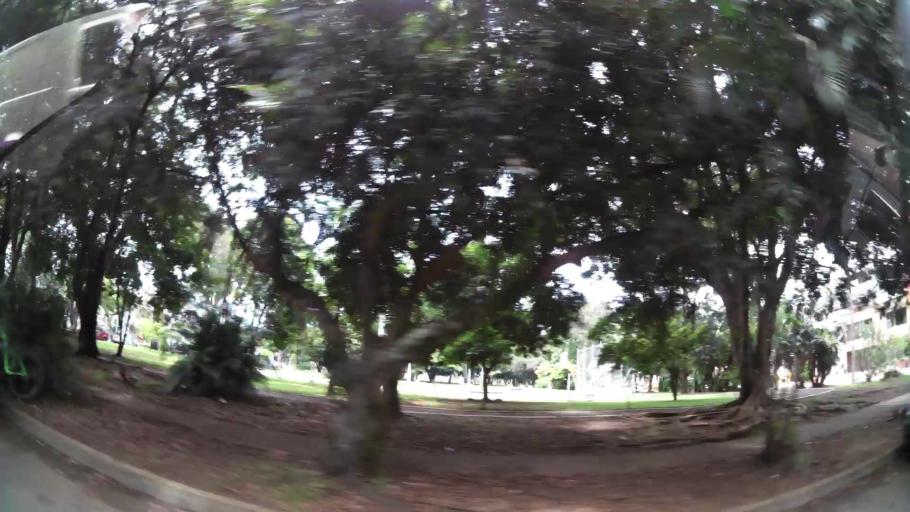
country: CO
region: Valle del Cauca
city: Cali
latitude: 3.3834
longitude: -76.5304
